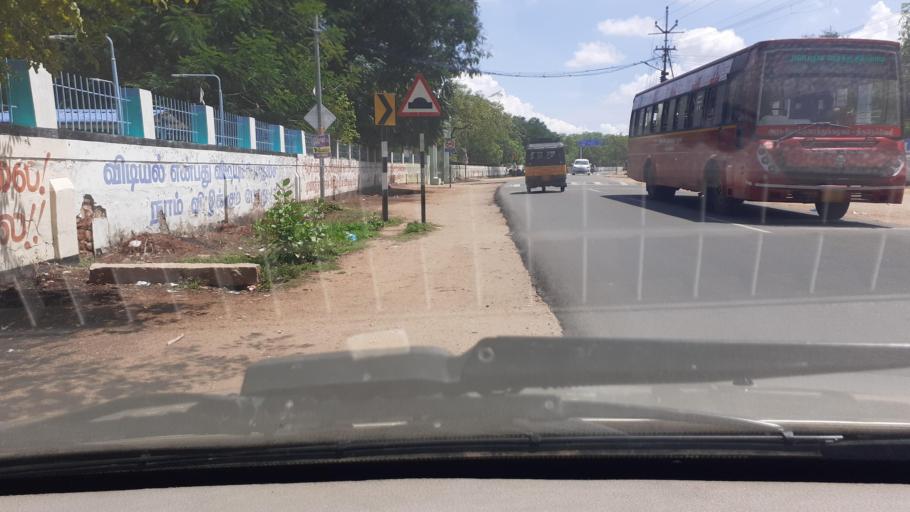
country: IN
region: Tamil Nadu
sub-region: Tirunelveli Kattabo
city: Tirunelveli
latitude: 8.7189
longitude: 77.7380
